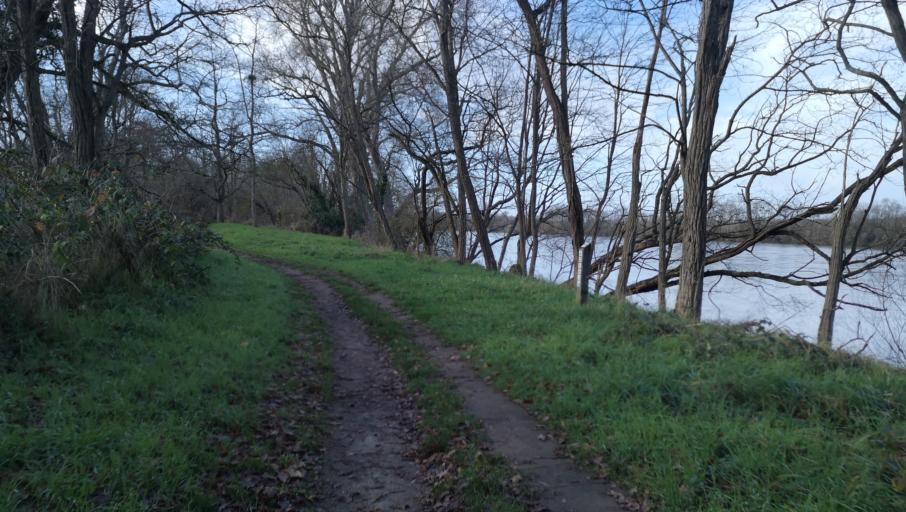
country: FR
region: Centre
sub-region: Departement du Loiret
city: Saint-Hilaire-Saint-Mesmin
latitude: 47.8702
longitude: 1.8180
